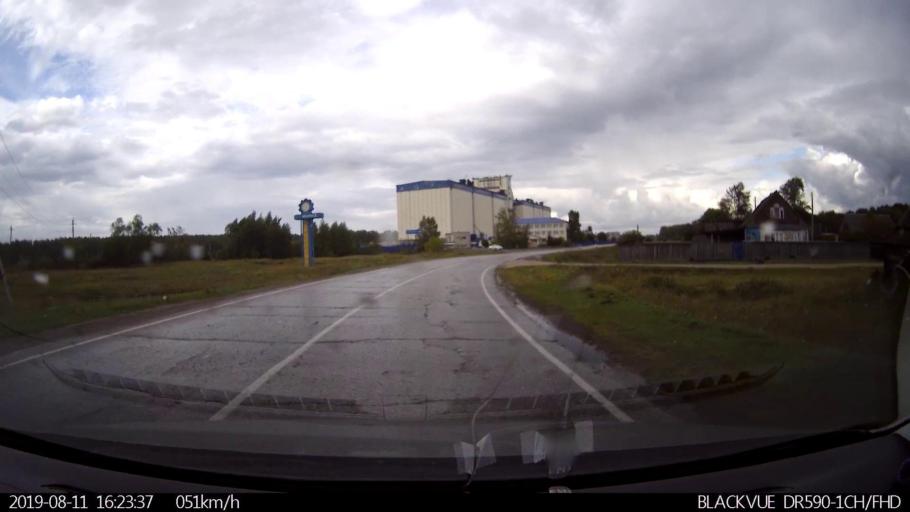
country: RU
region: Ulyanovsk
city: Mayna
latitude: 54.0964
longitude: 47.5885
